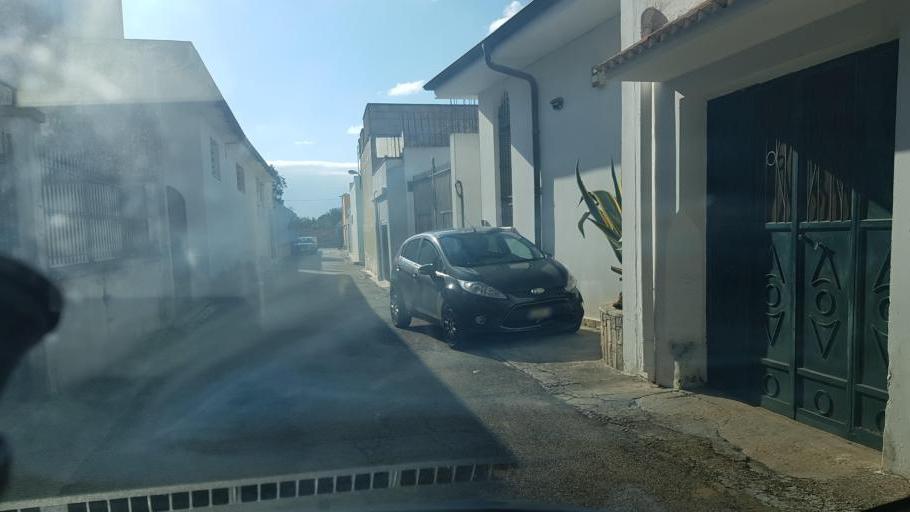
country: IT
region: Apulia
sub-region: Provincia di Brindisi
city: San Pietro Vernotico
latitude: 40.4830
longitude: 17.9916
